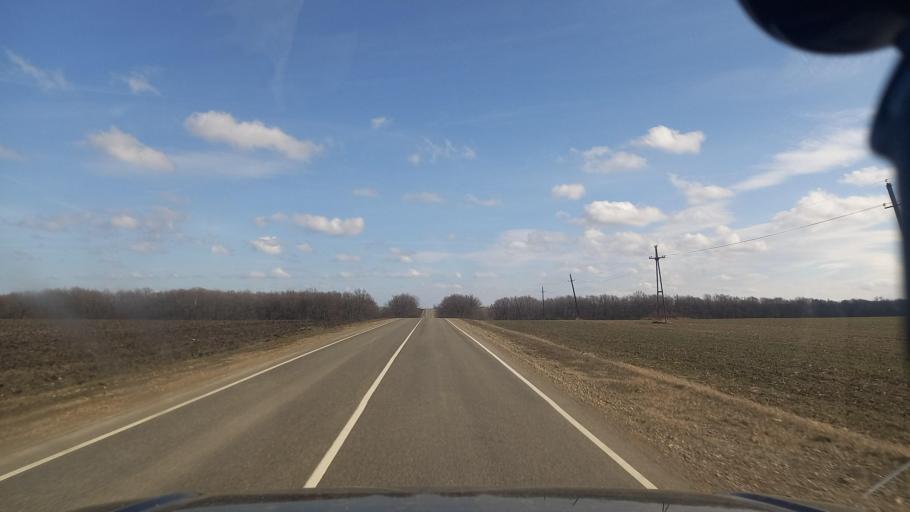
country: RU
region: Krasnodarskiy
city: Novodmitriyevskaya
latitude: 44.7950
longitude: 38.9339
